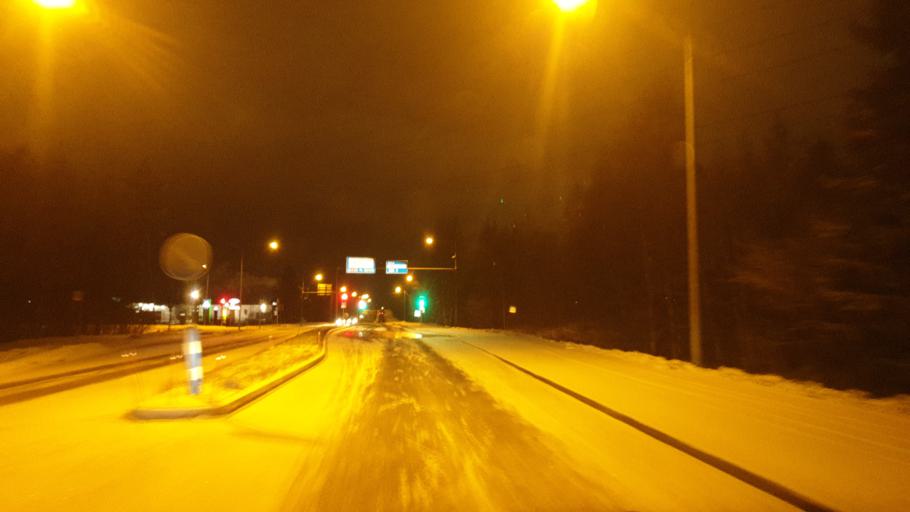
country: FI
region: Northern Ostrobothnia
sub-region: Oulu
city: Oulu
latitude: 64.9850
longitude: 25.4767
